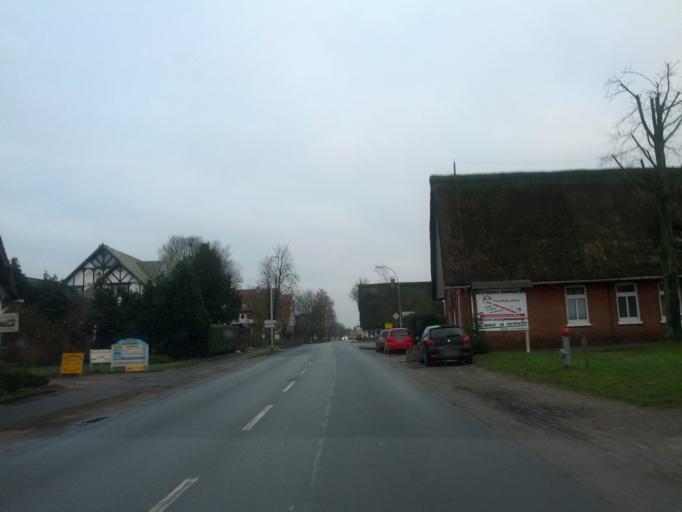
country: DE
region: Lower Saxony
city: Jork
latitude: 53.5315
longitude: 9.6869
